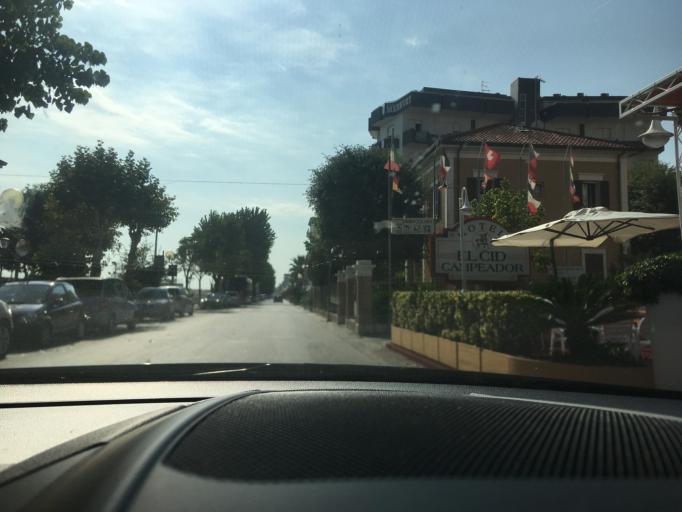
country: IT
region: Emilia-Romagna
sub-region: Provincia di Rimini
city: Santa Giustina
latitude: 44.1110
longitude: 12.5078
